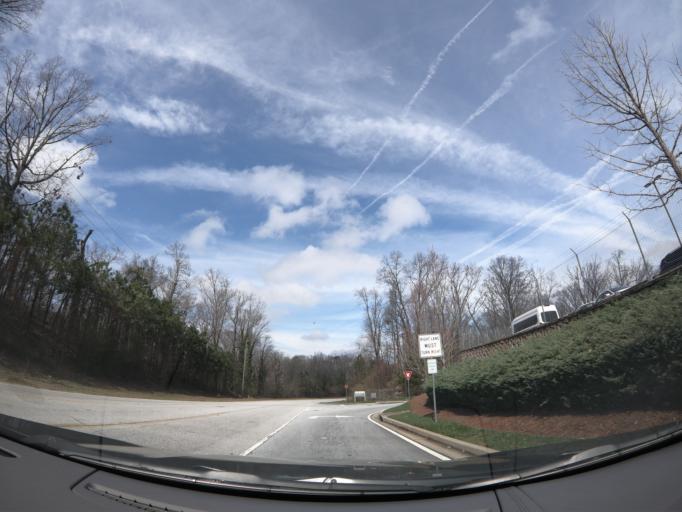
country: US
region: Georgia
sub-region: Fulton County
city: College Park
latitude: 33.6410
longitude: -84.4677
